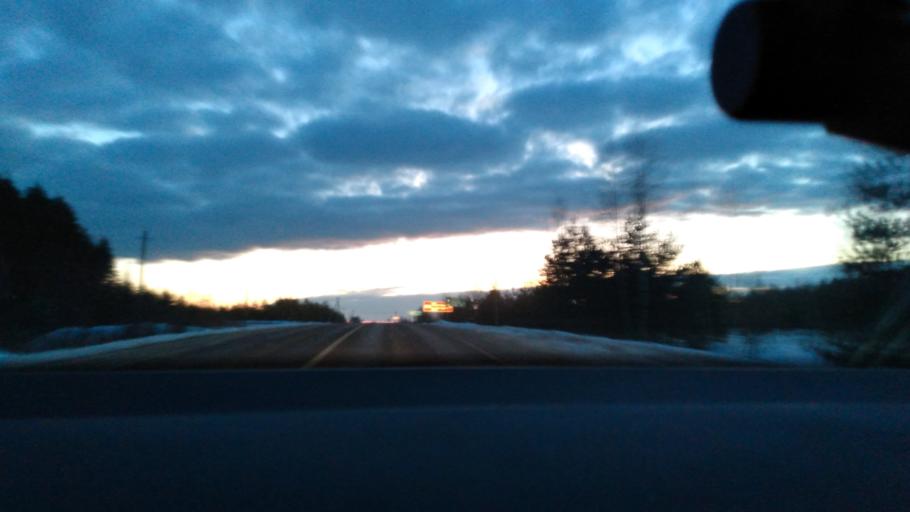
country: RU
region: Moskovskaya
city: Yegor'yevsk
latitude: 55.2535
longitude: 39.0666
